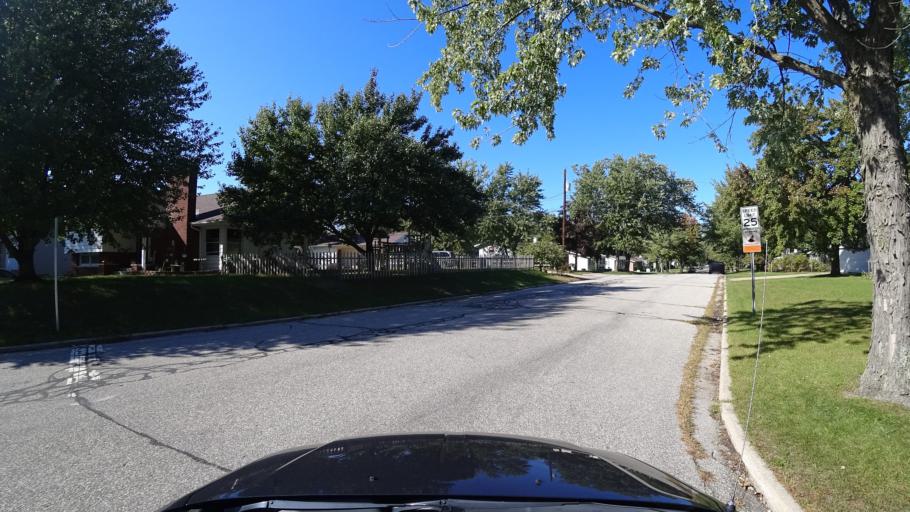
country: US
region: Indiana
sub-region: LaPorte County
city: Michigan City
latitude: 41.6926
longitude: -86.9081
